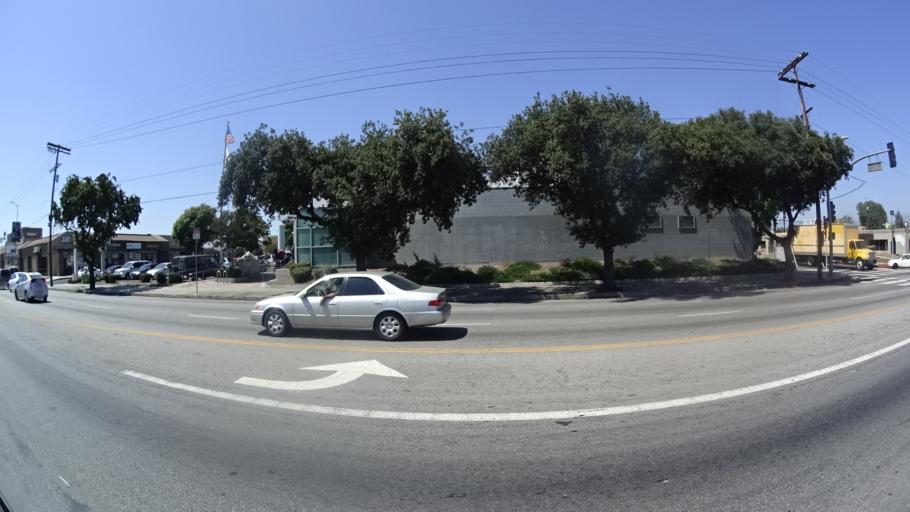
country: US
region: California
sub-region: Los Angeles County
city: Van Nuys
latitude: 34.2217
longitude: -118.4463
